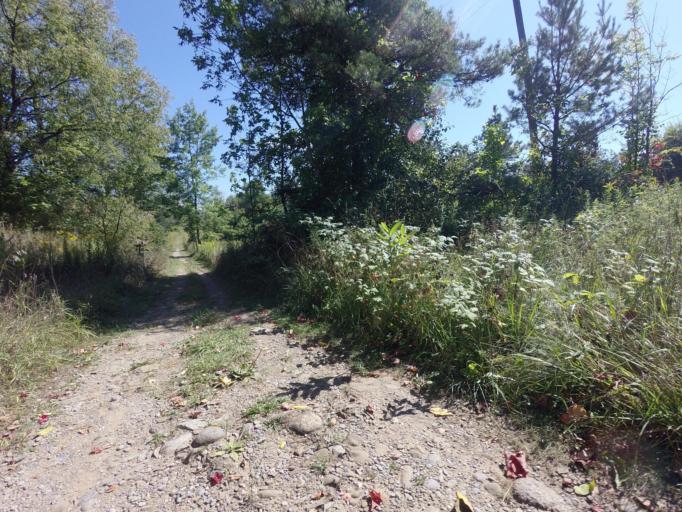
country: CA
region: Ontario
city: Orangeville
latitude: 43.8205
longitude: -80.0145
